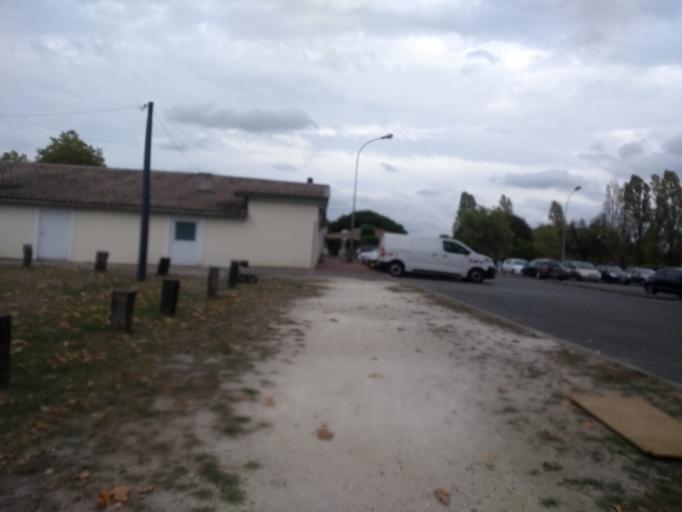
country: FR
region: Aquitaine
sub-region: Departement de la Gironde
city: Talence
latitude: 44.7882
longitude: -0.5938
